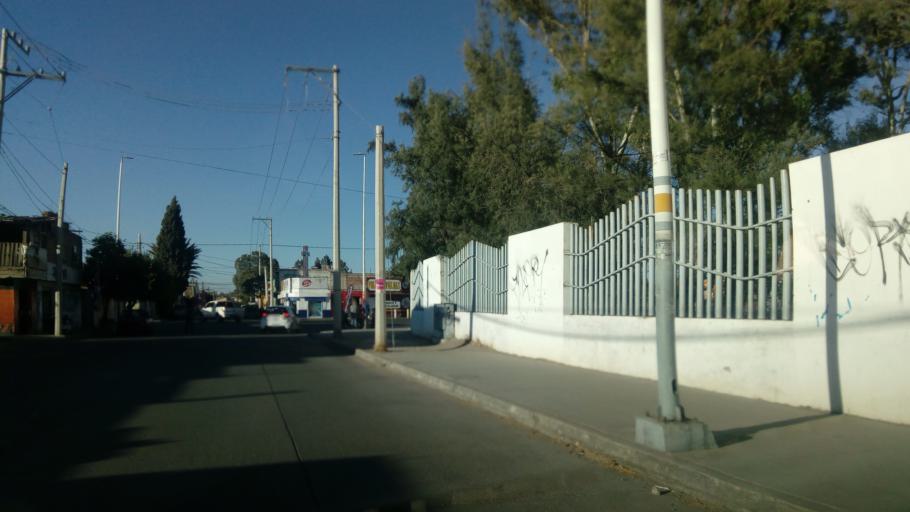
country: MX
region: Durango
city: Victoria de Durango
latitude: 23.9975
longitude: -104.6792
